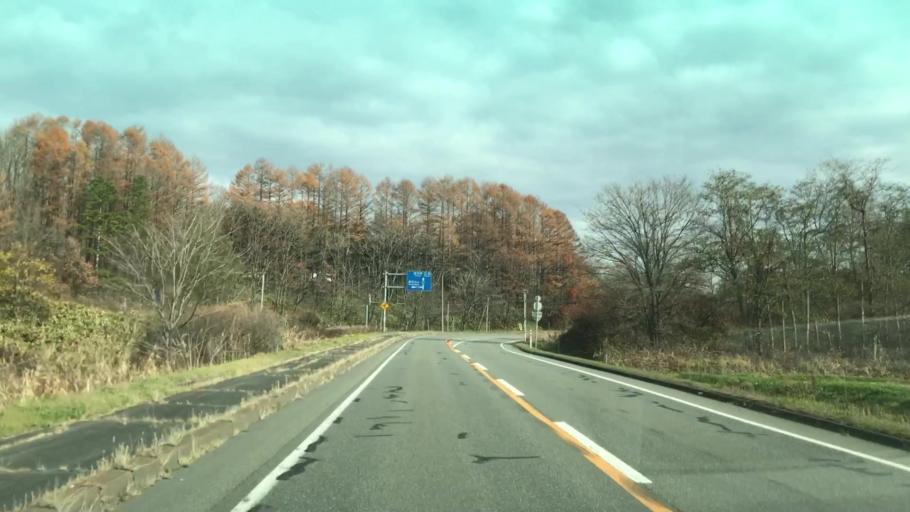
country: JP
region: Hokkaido
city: Shizunai-furukawacho
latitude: 42.7175
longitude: 142.2592
